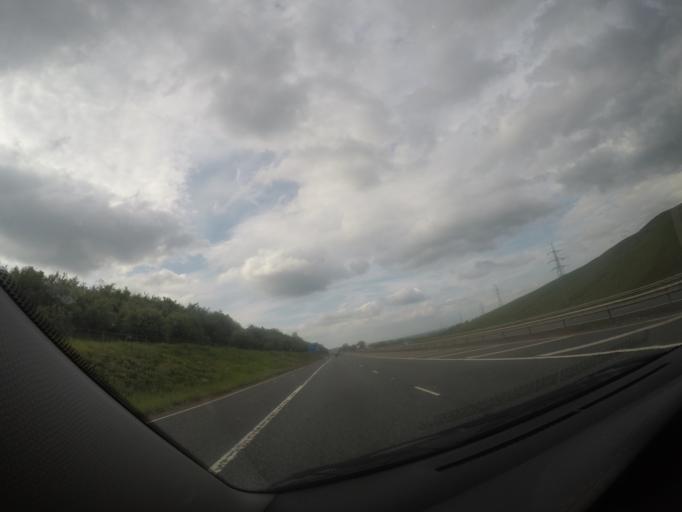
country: GB
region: Scotland
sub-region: South Lanarkshire
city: Douglas
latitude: 55.5606
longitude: -3.8042
